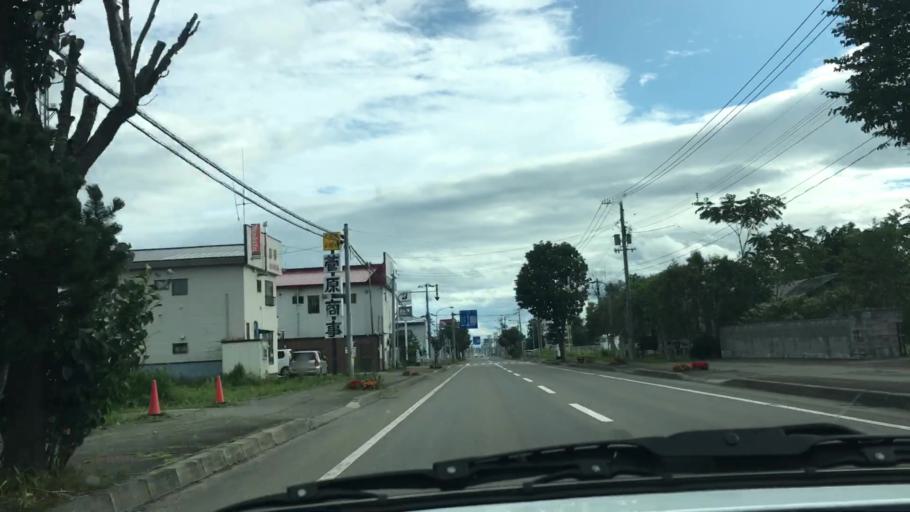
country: JP
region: Hokkaido
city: Otofuke
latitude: 43.2380
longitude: 143.2963
